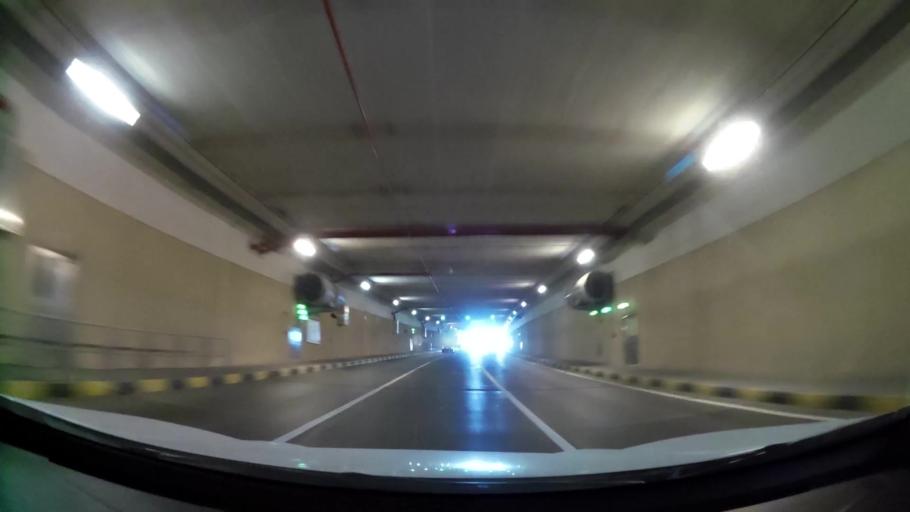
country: AE
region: Abu Dhabi
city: Abu Dhabi
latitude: 24.4616
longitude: 54.6112
